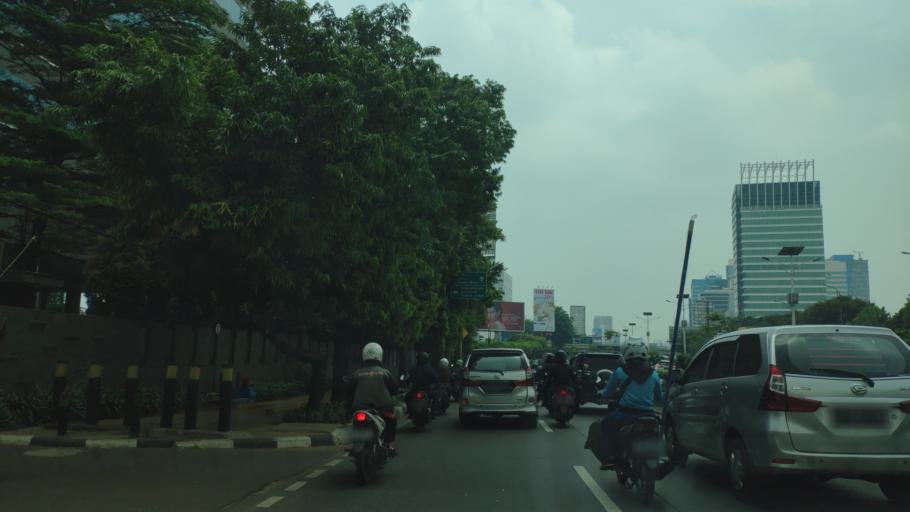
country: ID
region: Jakarta Raya
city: Jakarta
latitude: -6.1965
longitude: 106.7974
